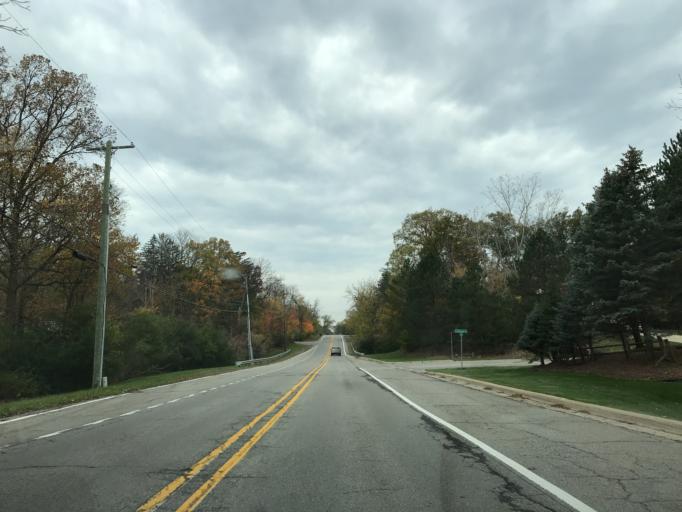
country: US
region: Michigan
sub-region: Oakland County
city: Franklin
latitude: 42.4714
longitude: -83.3068
